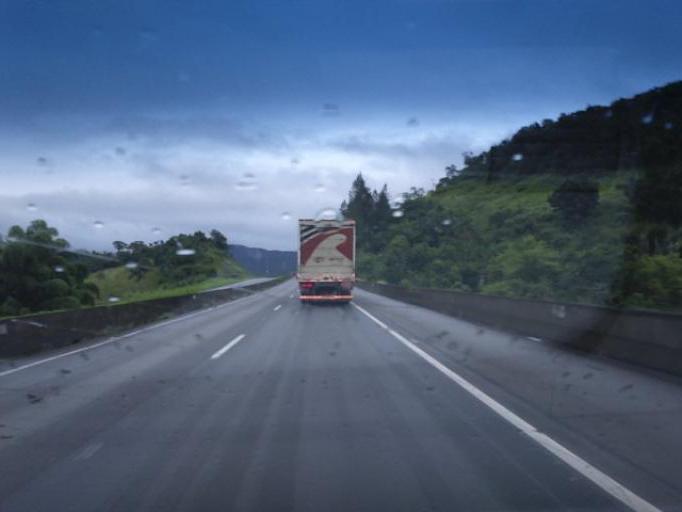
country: BR
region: Sao Paulo
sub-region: Miracatu
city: Miracatu
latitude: -24.1714
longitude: -47.3402
